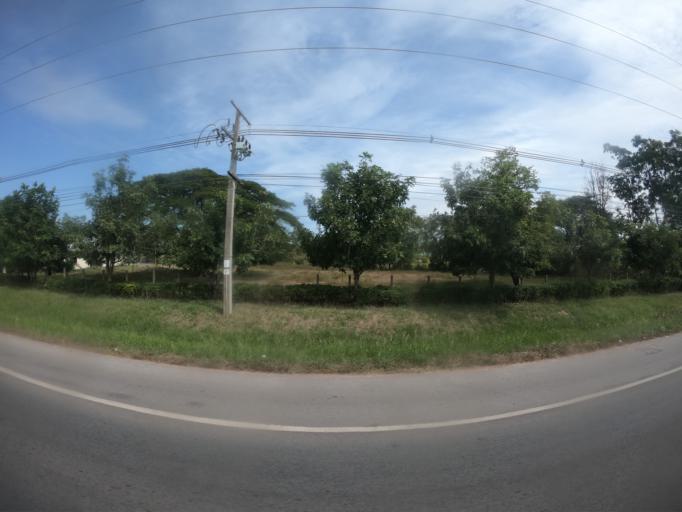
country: TH
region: Maha Sarakham
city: Chiang Yuen
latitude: 16.4442
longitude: 103.0398
